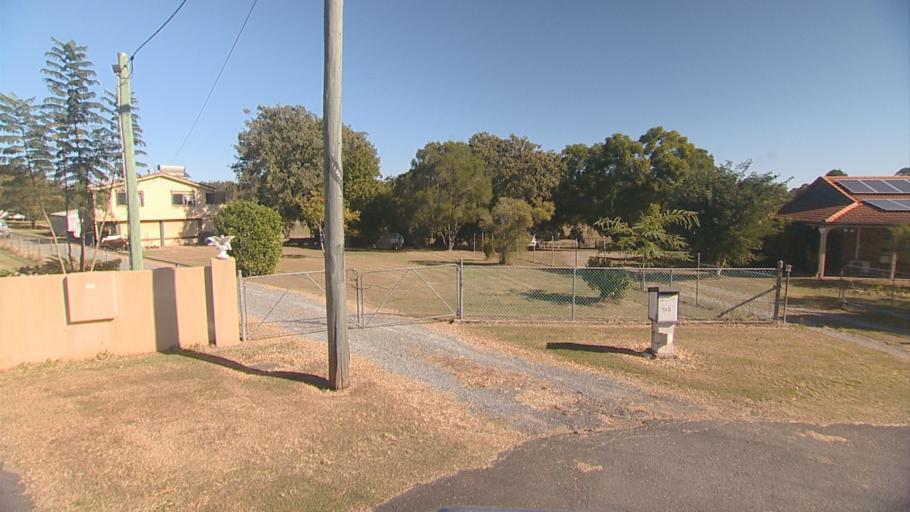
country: AU
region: Queensland
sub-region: Logan
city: North Maclean
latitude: -27.7859
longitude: 153.0204
